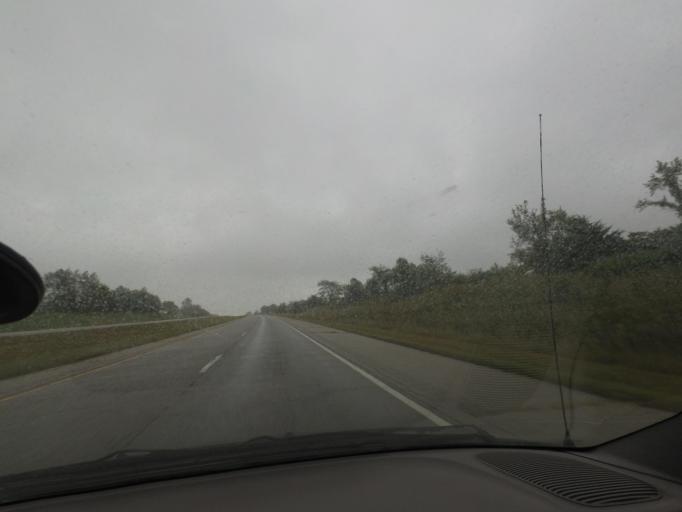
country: US
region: Illinois
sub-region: Pike County
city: Barry
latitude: 39.6924
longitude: -90.9942
